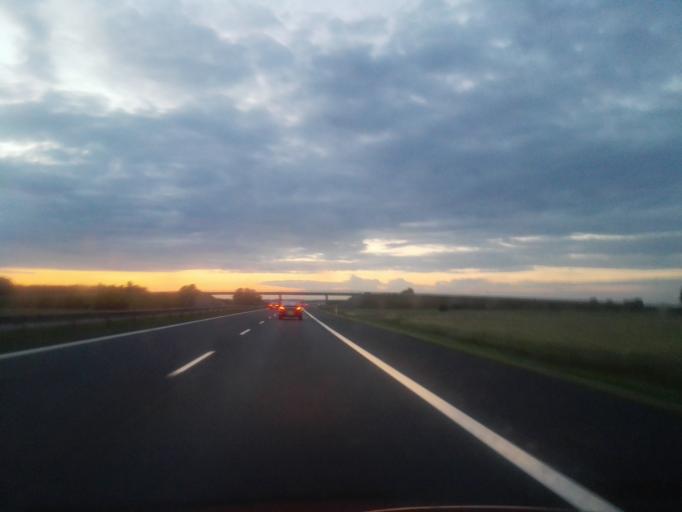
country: PL
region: Lodz Voivodeship
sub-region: Powiat piotrkowski
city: Grabica
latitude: 51.5069
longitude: 19.6036
